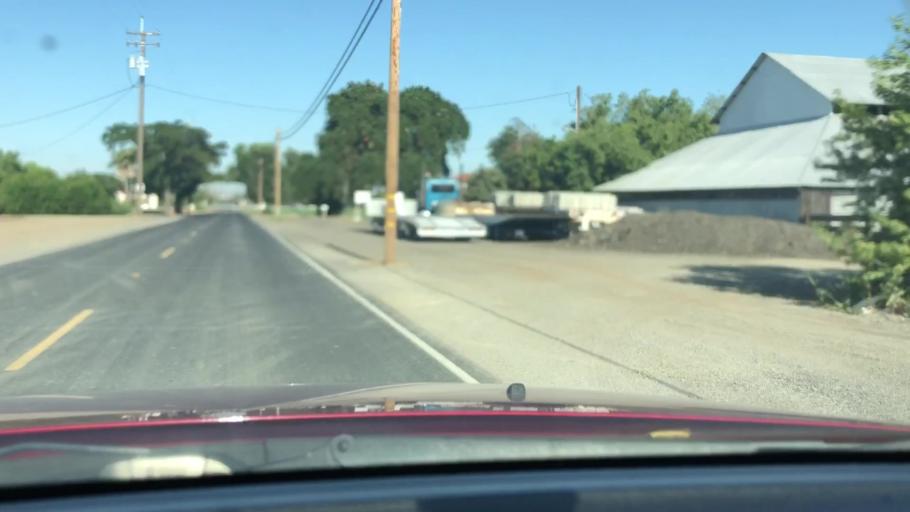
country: US
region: California
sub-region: San Joaquin County
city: Tracy
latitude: 37.7253
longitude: -121.4106
